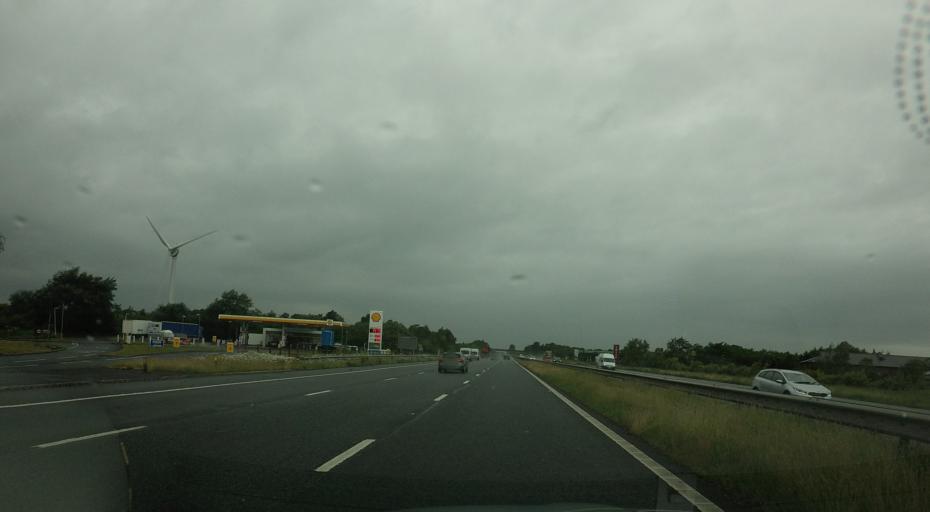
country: GB
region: England
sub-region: Cumbria
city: Carlisle
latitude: 54.9504
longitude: -2.9782
